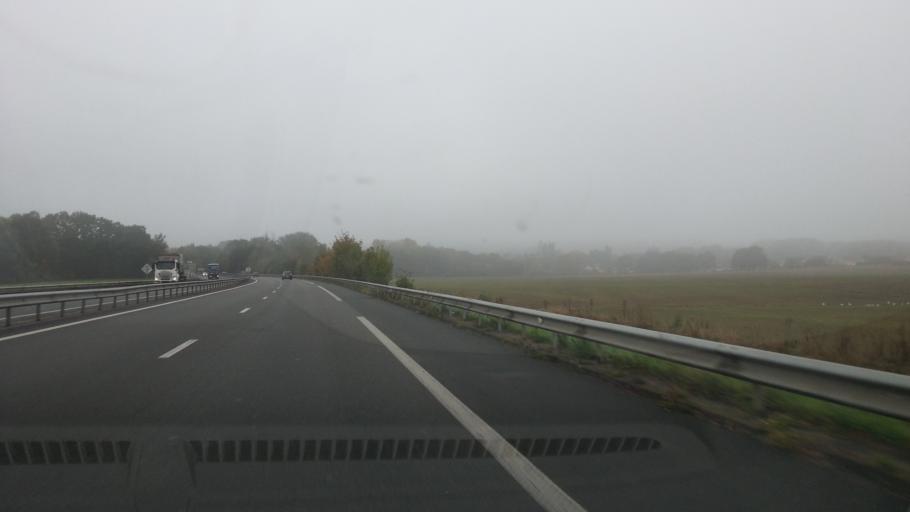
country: FR
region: Picardie
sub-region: Departement de l'Oise
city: Breuil-le-Vert
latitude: 49.3678
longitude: 2.4295
